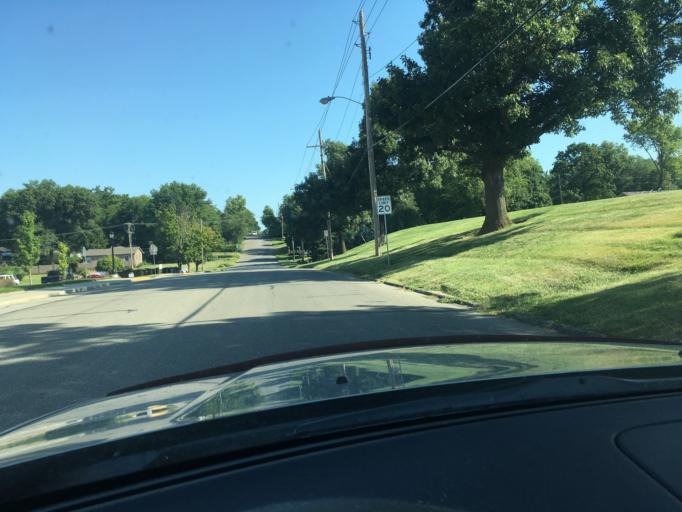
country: US
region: Kansas
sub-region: Atchison County
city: Atchison
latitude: 39.5771
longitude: -95.1152
